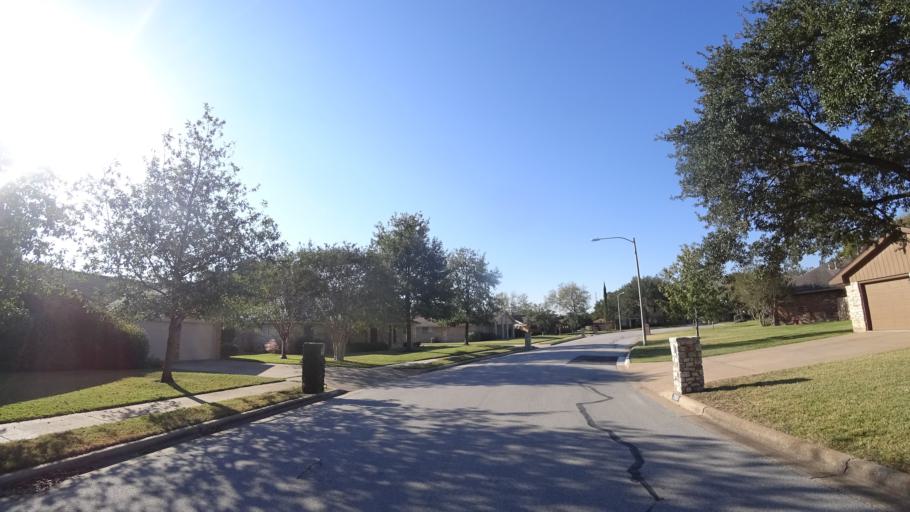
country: US
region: Texas
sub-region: Travis County
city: Shady Hollow
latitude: 30.2202
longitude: -97.8498
